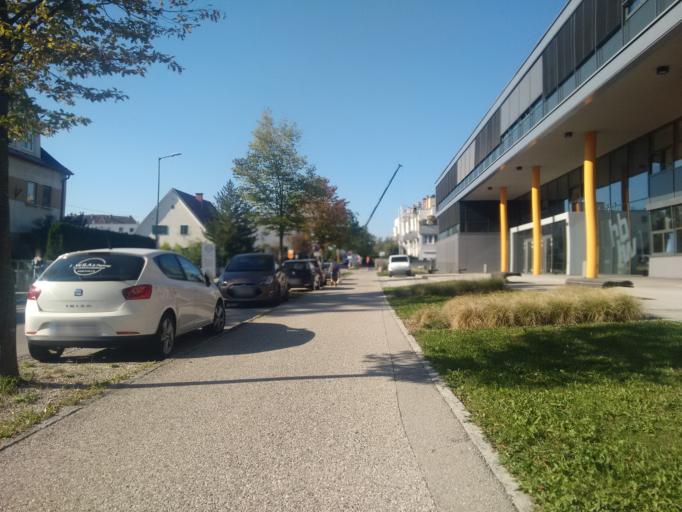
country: AT
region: Upper Austria
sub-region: Wels Stadt
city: Wels
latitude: 48.1716
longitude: 14.0198
